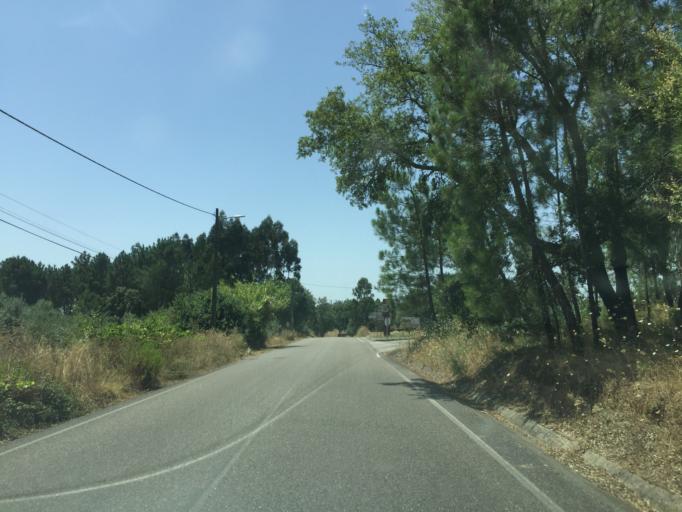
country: PT
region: Santarem
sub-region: Ferreira do Zezere
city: Ferreira do Zezere
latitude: 39.6245
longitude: -8.3101
